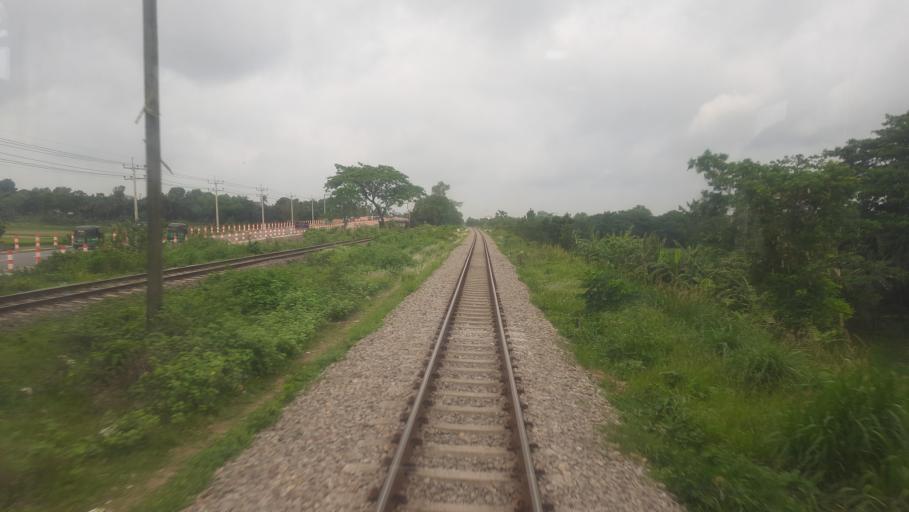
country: BD
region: Dhaka
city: Narsingdi
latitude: 23.9318
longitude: 90.7404
